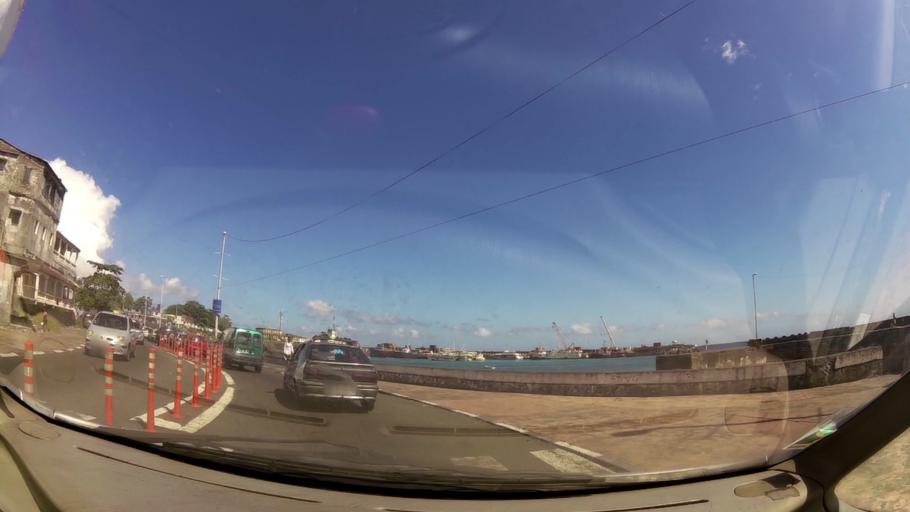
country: KM
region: Grande Comore
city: Moroni
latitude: -11.7036
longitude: 43.2514
